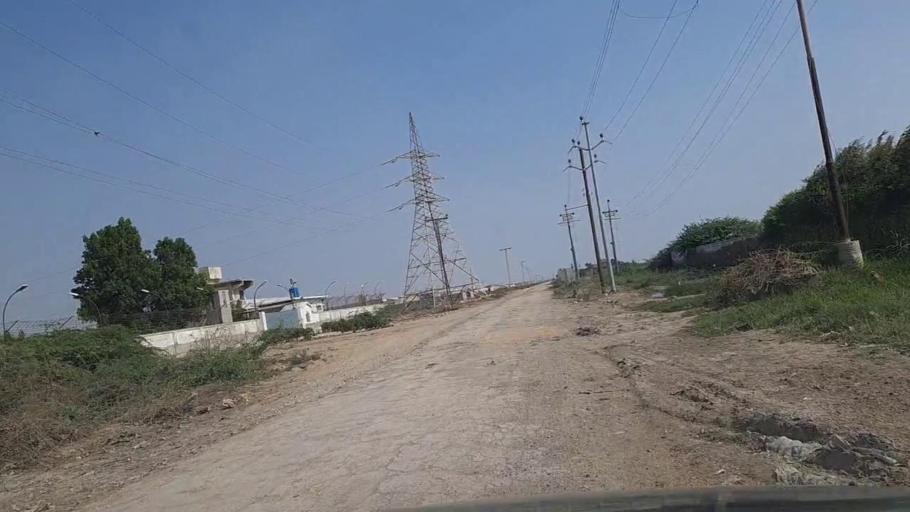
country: PK
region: Sindh
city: Gharo
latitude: 24.7384
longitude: 67.6073
